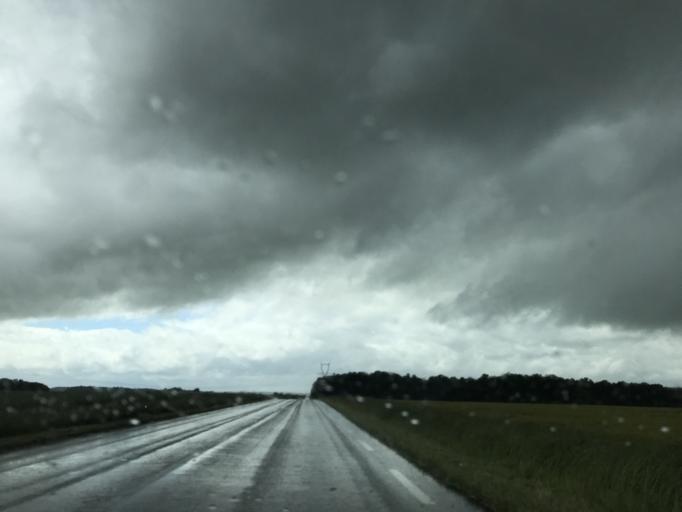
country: FR
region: Haute-Normandie
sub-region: Departement de l'Eure
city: Damville
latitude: 48.8765
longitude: 1.1084
